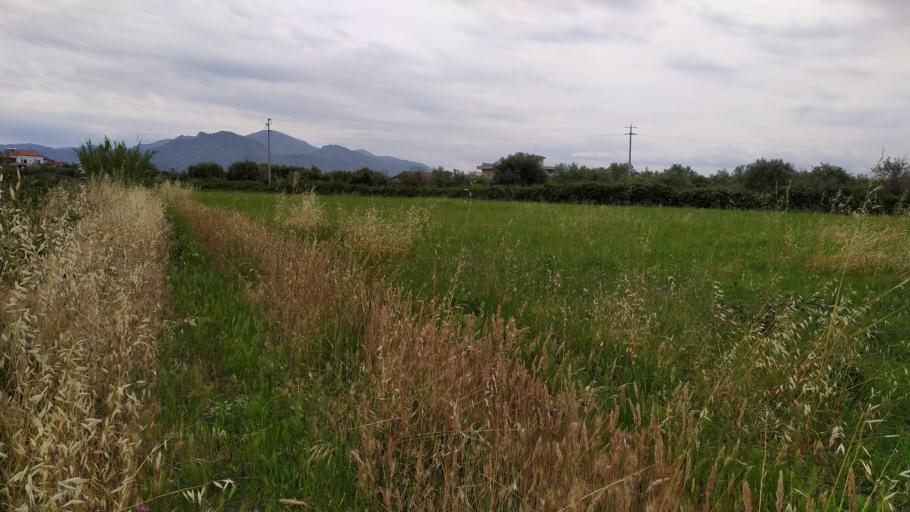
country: IT
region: Sicily
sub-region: Messina
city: San Filippo del Mela
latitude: 38.1848
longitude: 15.2617
